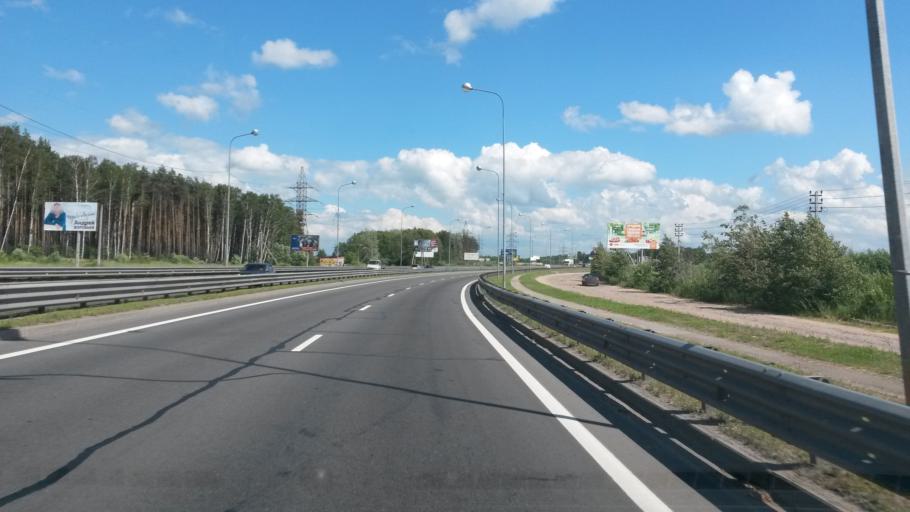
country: RU
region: Jaroslavl
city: Yaroslavl
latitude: 57.6836
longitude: 39.8818
